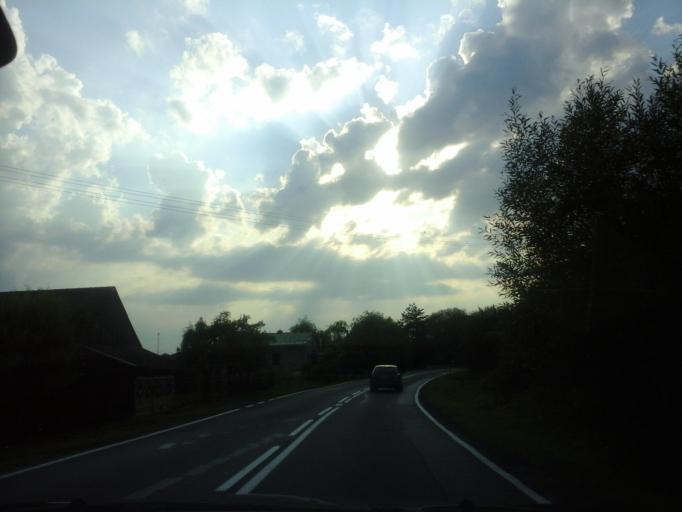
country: PL
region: Lesser Poland Voivodeship
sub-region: Powiat wadowicki
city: Laczany
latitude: 49.9656
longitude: 19.5739
